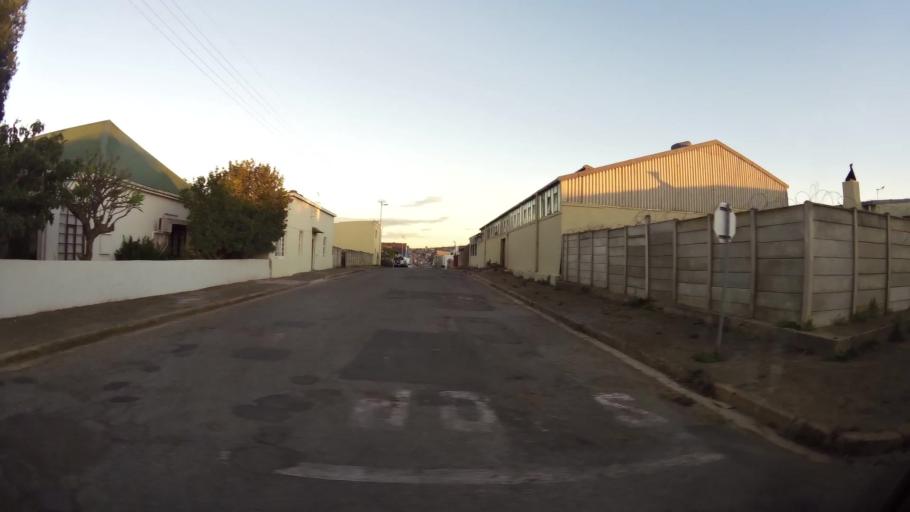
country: ZA
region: Western Cape
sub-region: Eden District Municipality
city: Riversdale
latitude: -34.0886
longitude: 21.2608
